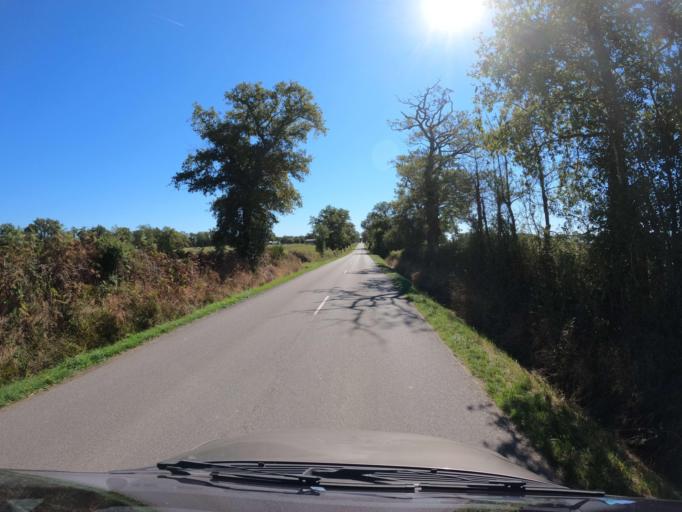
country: FR
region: Poitou-Charentes
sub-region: Departement de la Vienne
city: Lathus-Saint-Remy
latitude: 46.2728
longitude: 1.0219
